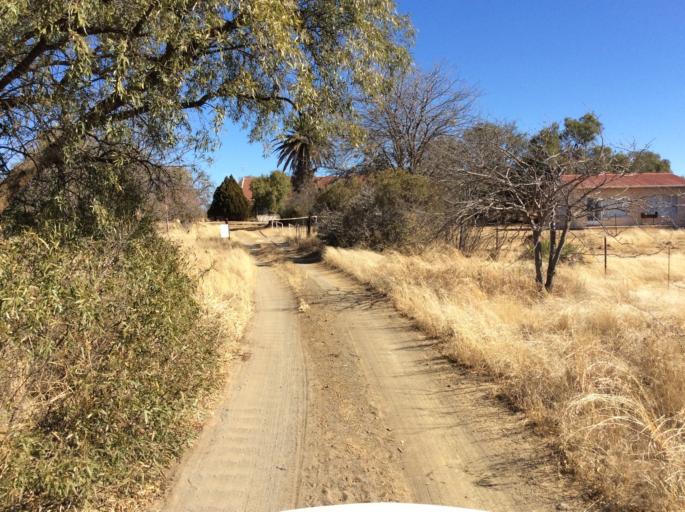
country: ZA
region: Orange Free State
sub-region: Lejweleputswa District Municipality
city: Brandfort
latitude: -28.7217
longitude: 26.0528
